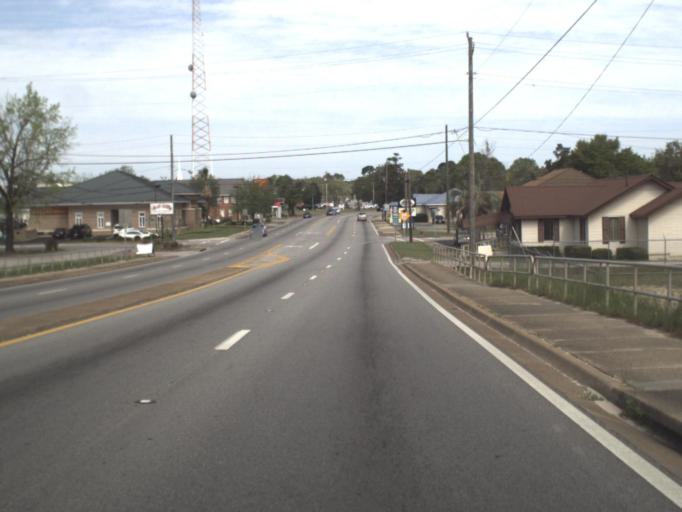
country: US
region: Florida
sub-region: Okaloosa County
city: Crestview
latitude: 30.7593
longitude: -86.5690
